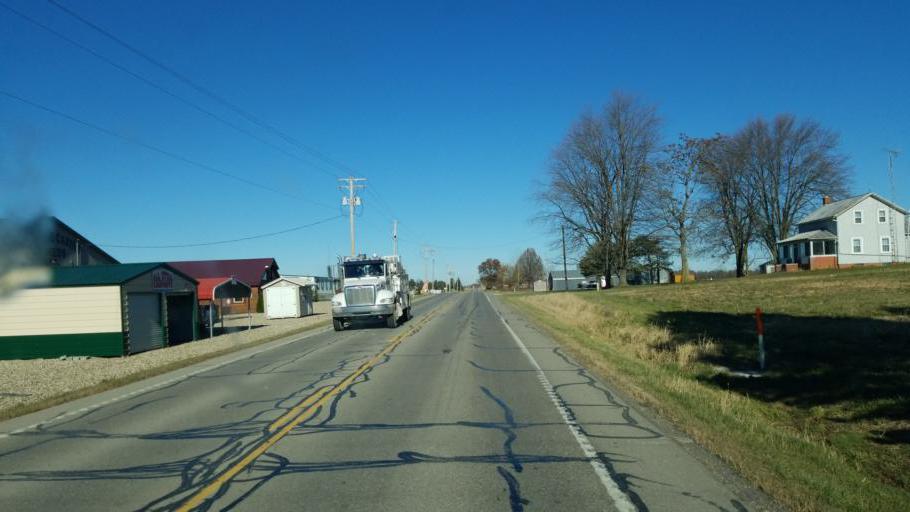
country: US
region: Ohio
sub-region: Huron County
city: Greenwich
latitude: 40.9578
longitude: -82.4951
